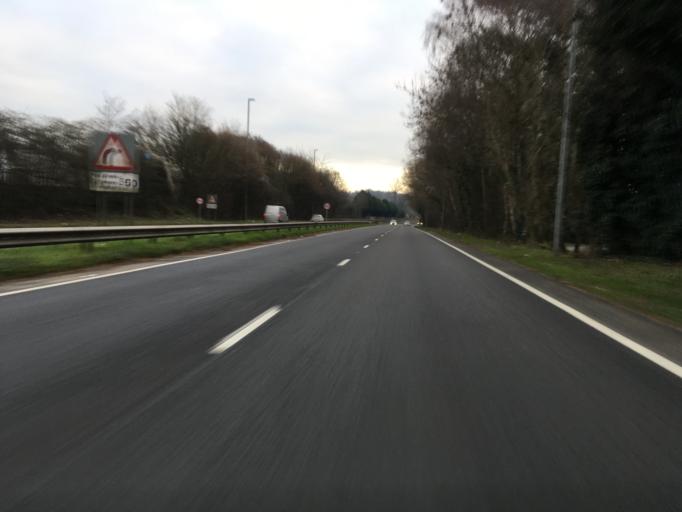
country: GB
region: Wales
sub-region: Newport
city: Newport
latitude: 51.5830
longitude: -3.0477
